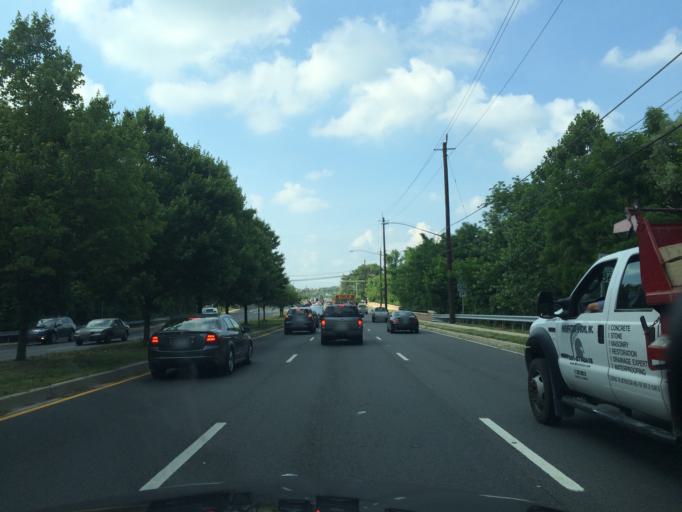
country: US
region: Maryland
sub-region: Montgomery County
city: North Kensington
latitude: 39.0488
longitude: -77.0754
